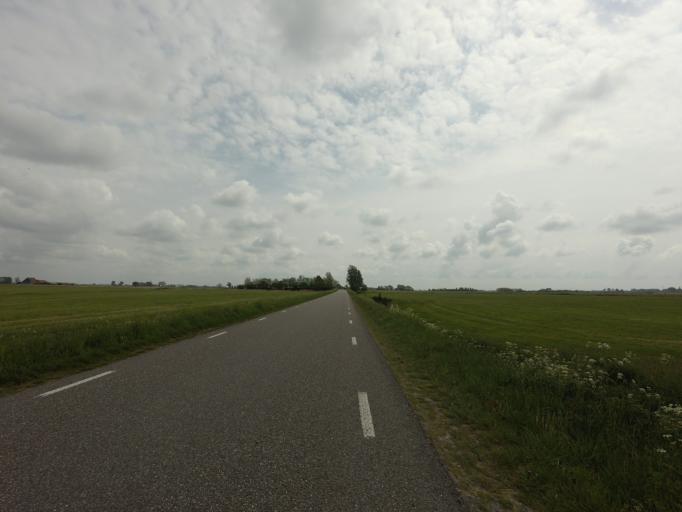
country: NL
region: Friesland
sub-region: Sudwest Fryslan
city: Bolsward
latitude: 53.0973
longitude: 5.5259
